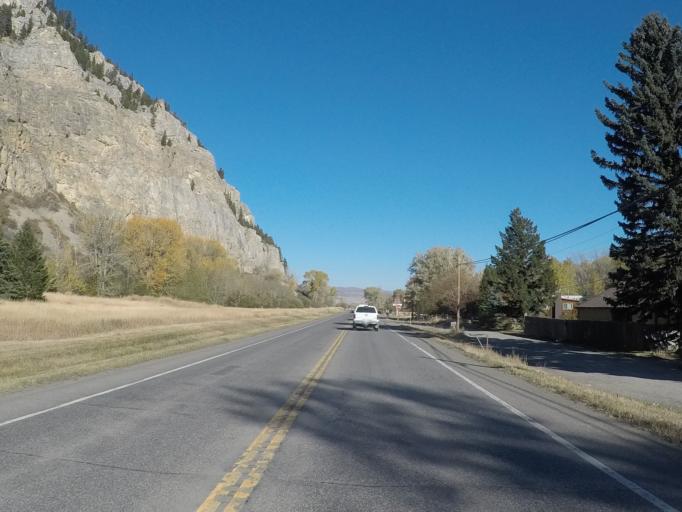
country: US
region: Montana
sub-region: Park County
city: Livingston
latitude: 45.6072
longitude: -110.5756
